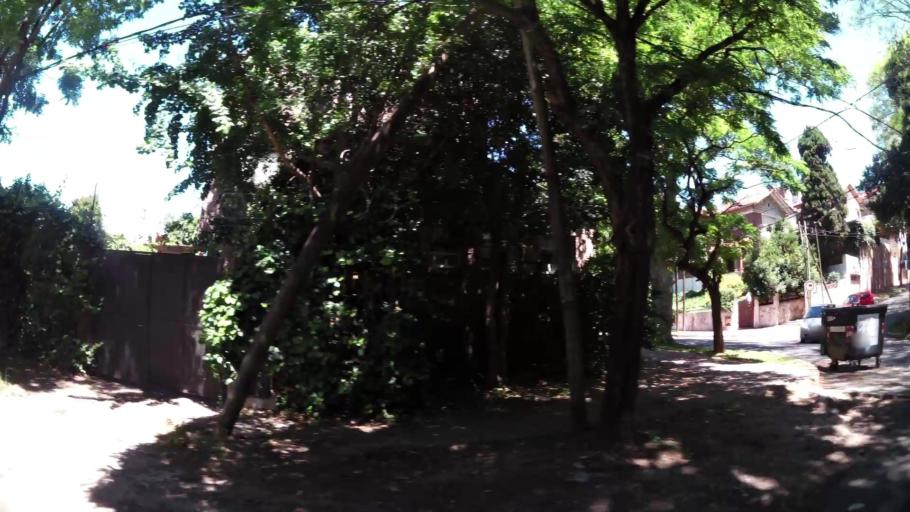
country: AR
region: Buenos Aires
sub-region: Partido de San Isidro
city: San Isidro
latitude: -34.4517
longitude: -58.5235
